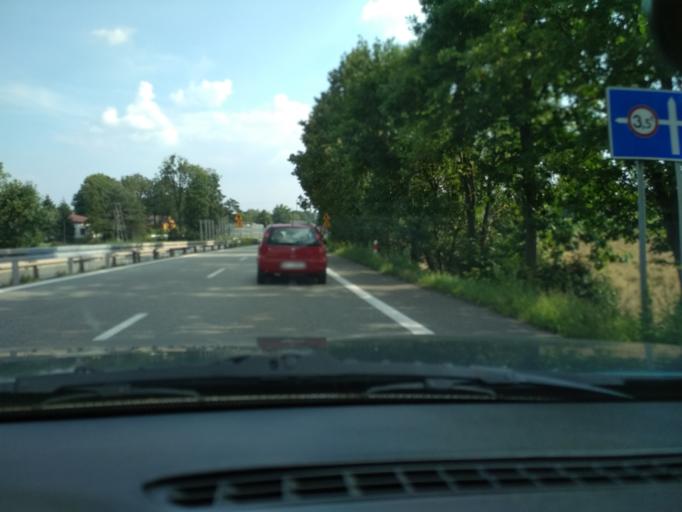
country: PL
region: Silesian Voivodeship
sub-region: Powiat pszczynski
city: Pawlowice
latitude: 49.9989
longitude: 18.7114
